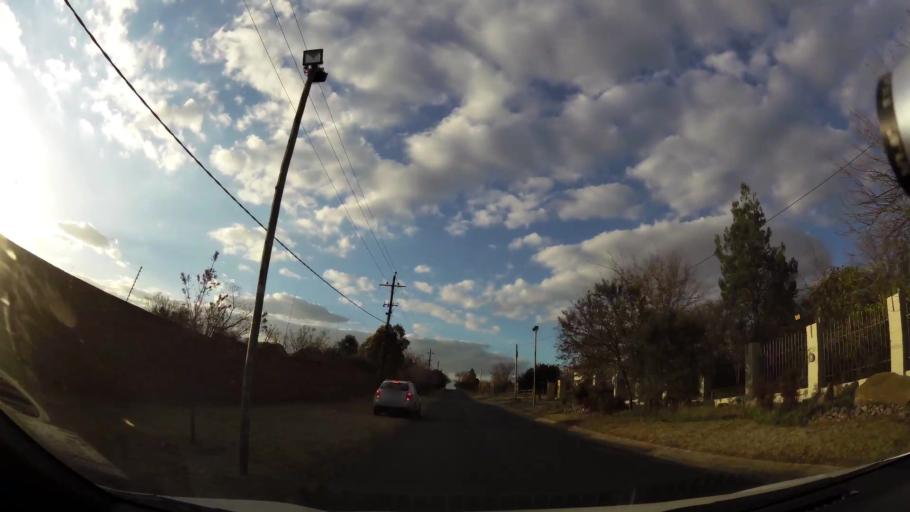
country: ZA
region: Gauteng
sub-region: City of Johannesburg Metropolitan Municipality
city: Diepsloot
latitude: -25.9989
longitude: 27.9680
